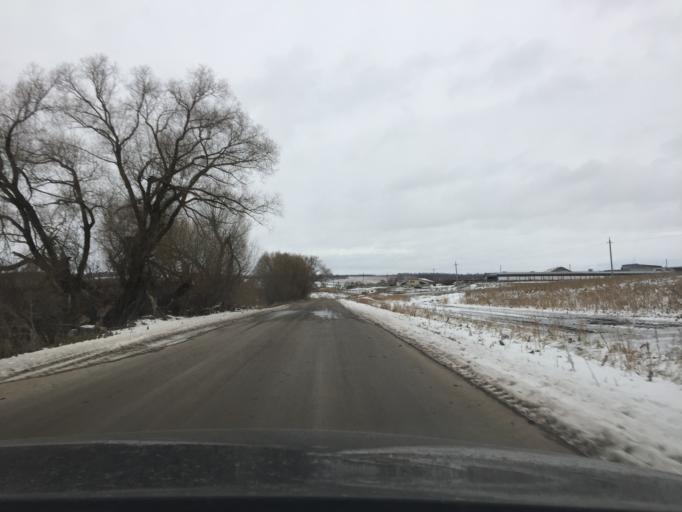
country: RU
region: Tula
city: Shchekino
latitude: 53.8336
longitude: 37.5673
